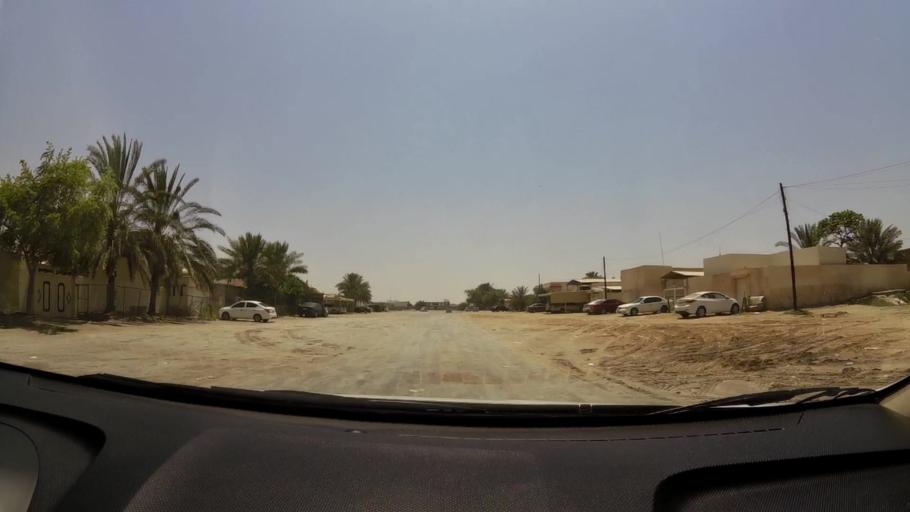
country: AE
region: Umm al Qaywayn
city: Umm al Qaywayn
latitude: 25.5039
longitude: 55.5730
